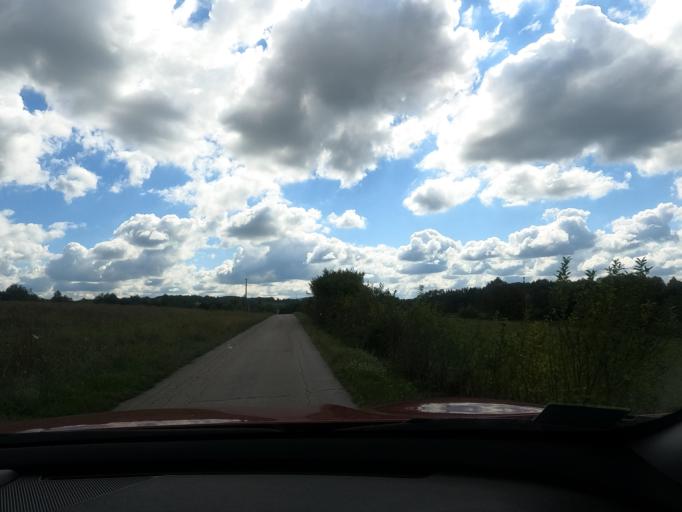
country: BA
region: Federation of Bosnia and Herzegovina
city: Velika Kladusa
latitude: 45.2171
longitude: 15.7119
